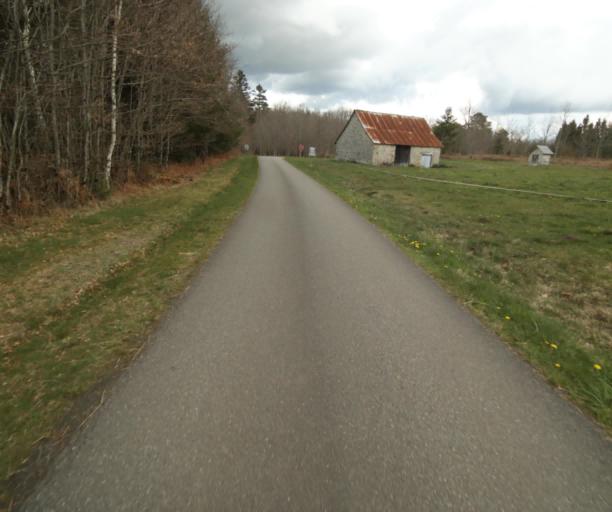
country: FR
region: Limousin
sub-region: Departement de la Correze
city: Correze
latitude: 45.2627
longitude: 1.9051
